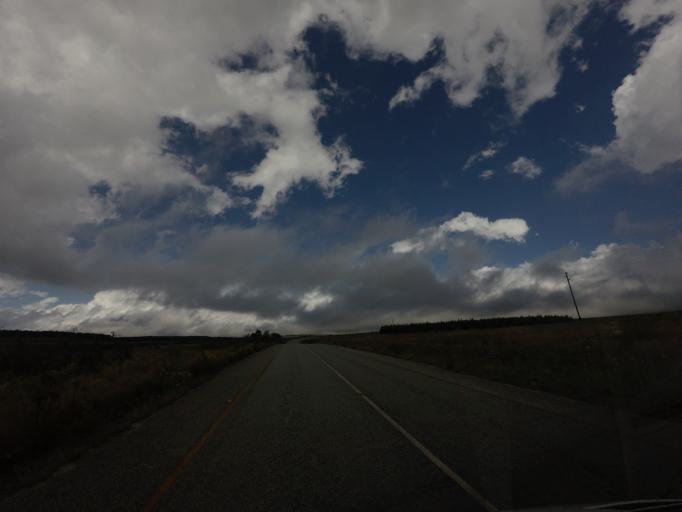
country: ZA
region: Mpumalanga
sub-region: Ehlanzeni District
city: Graksop
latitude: -24.8585
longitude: 30.8684
